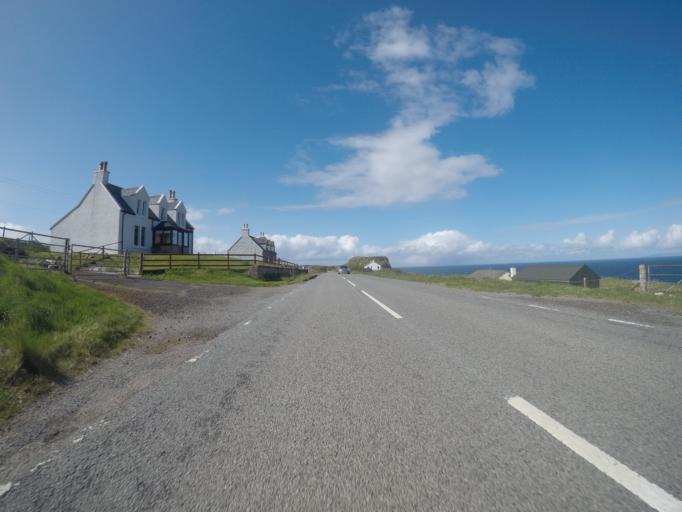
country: GB
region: Scotland
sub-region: Highland
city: Portree
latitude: 57.5958
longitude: -6.1612
